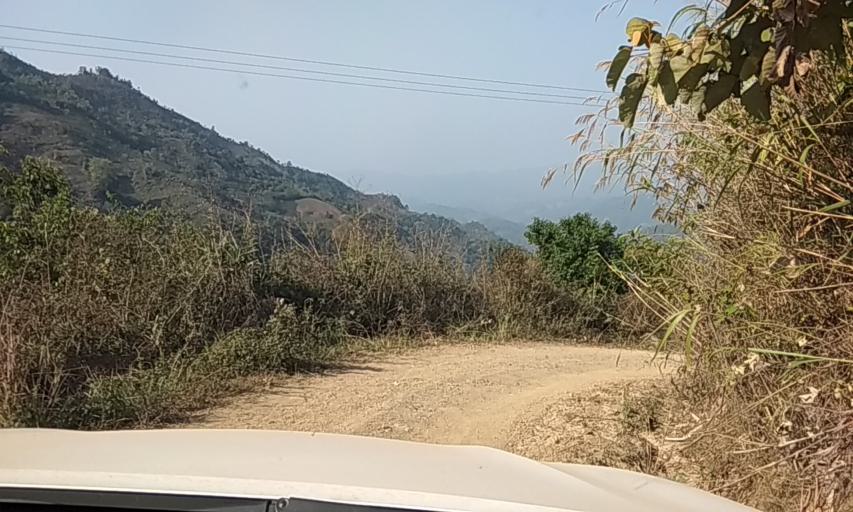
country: LA
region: Phongsali
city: Phongsali
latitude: 21.6908
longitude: 102.1001
